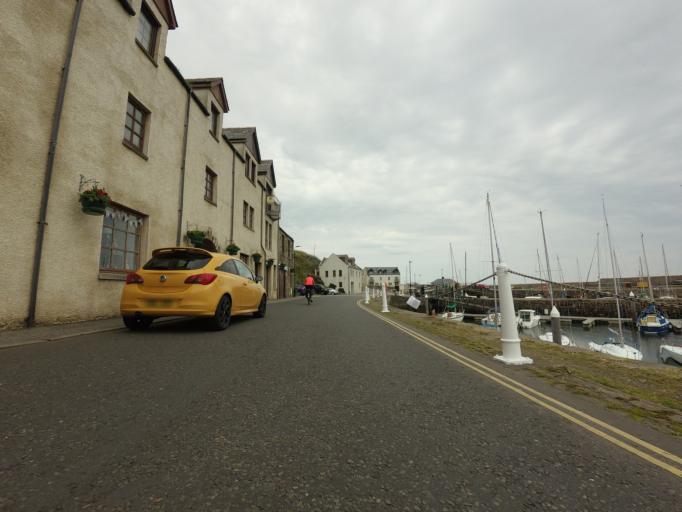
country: GB
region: Scotland
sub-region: Aberdeenshire
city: Banff
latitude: 57.6694
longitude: -2.5231
